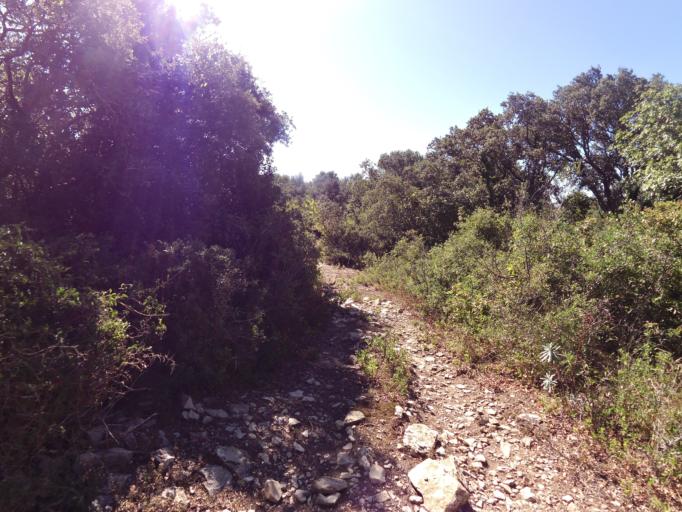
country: FR
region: Languedoc-Roussillon
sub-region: Departement du Gard
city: Congenies
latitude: 43.7621
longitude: 4.1833
